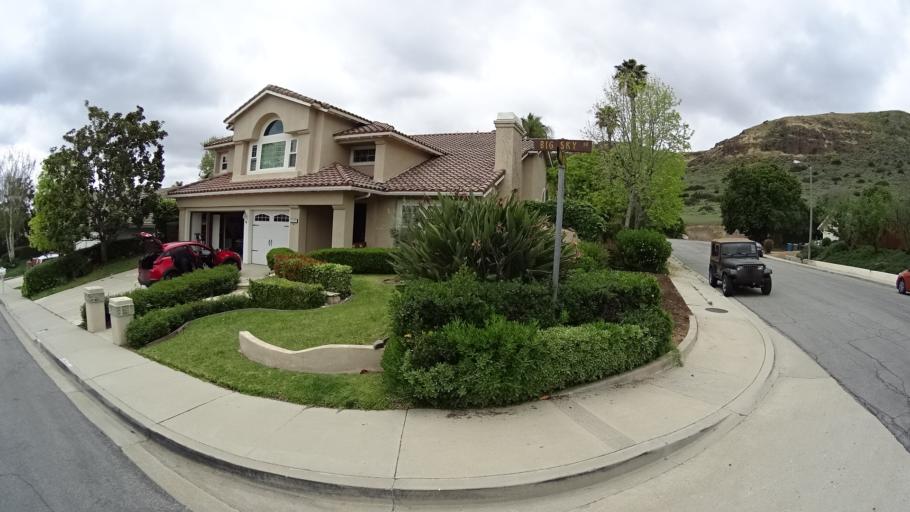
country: US
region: California
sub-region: Ventura County
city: Casa Conejo
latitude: 34.2223
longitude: -118.9018
